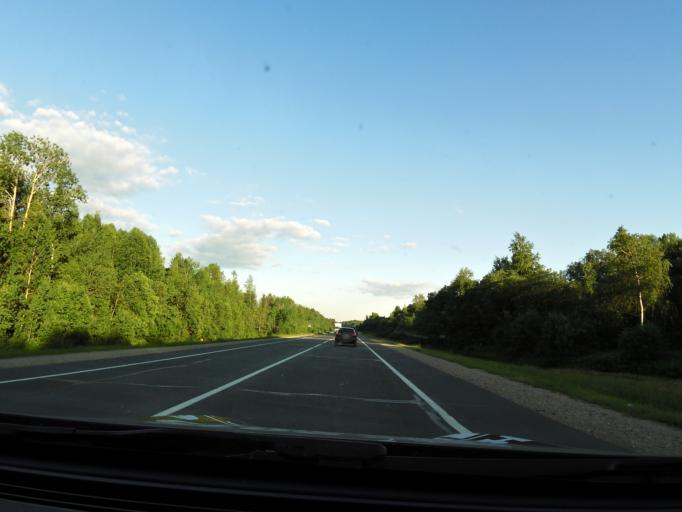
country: RU
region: Vologda
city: Vologda
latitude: 59.0911
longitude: 40.0023
